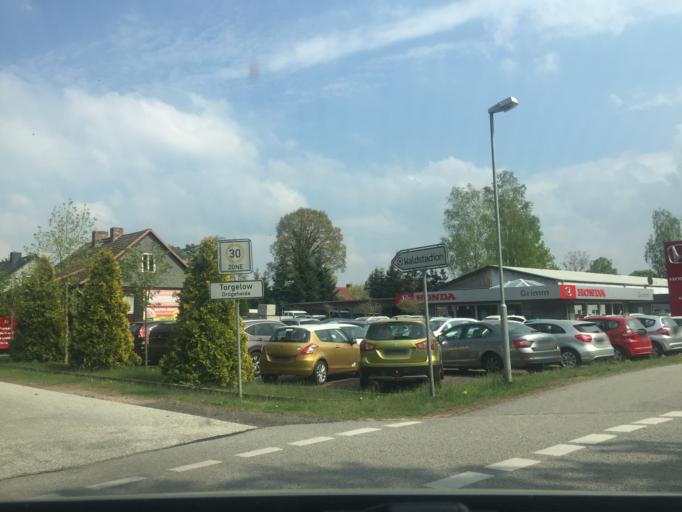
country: DE
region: Mecklenburg-Vorpommern
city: Torgelow
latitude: 53.6141
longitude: 14.0354
